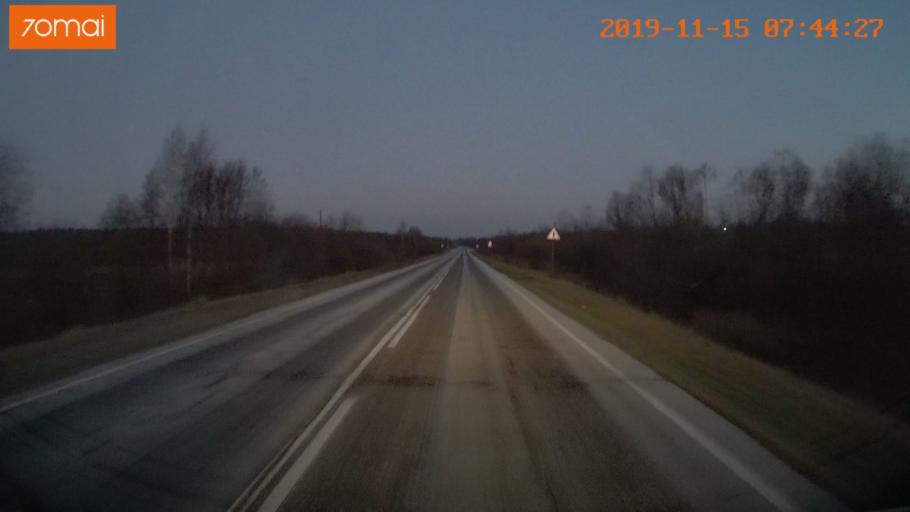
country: RU
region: Vologda
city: Sheksna
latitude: 58.8135
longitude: 38.3128
